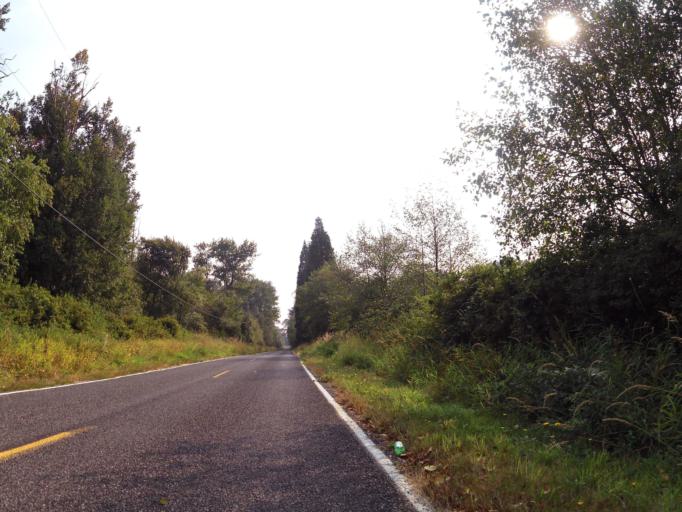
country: US
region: Washington
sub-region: Whatcom County
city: Birch Bay
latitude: 48.8631
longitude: -122.7183
